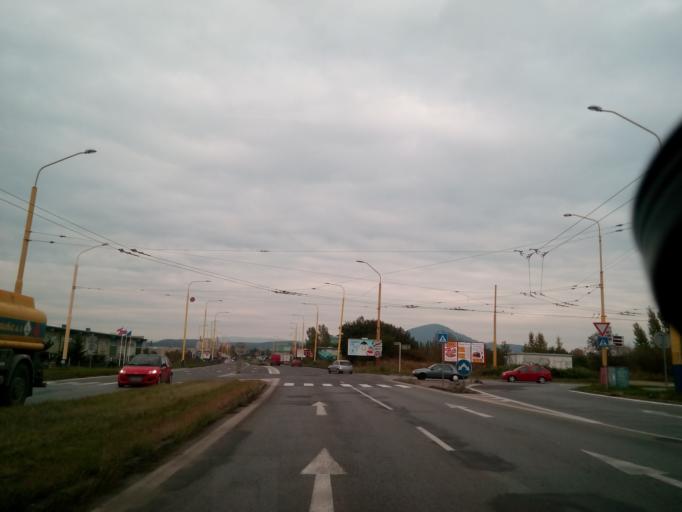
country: SK
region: Presovsky
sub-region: Okres Presov
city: Presov
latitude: 48.9998
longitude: 21.2698
